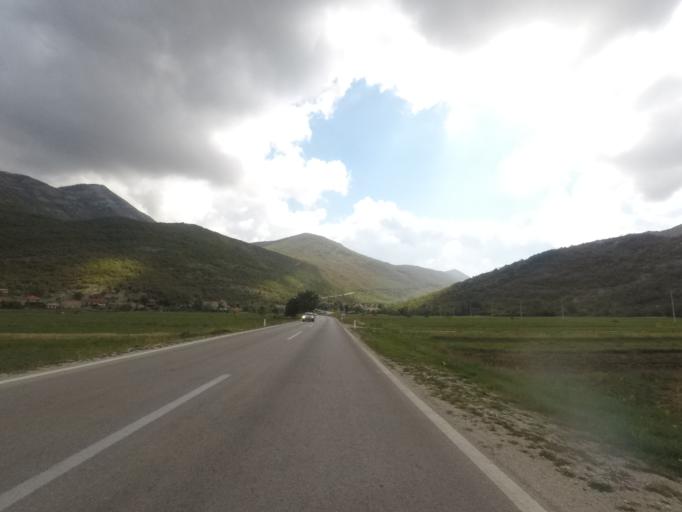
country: BA
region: Republika Srpska
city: Trebinje
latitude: 42.6078
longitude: 18.4207
